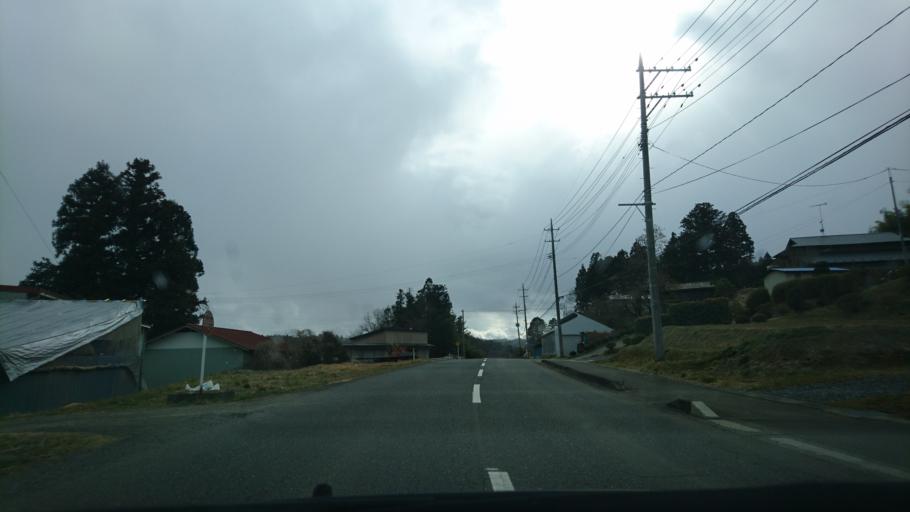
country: JP
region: Iwate
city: Ichinoseki
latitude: 38.8256
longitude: 141.1731
